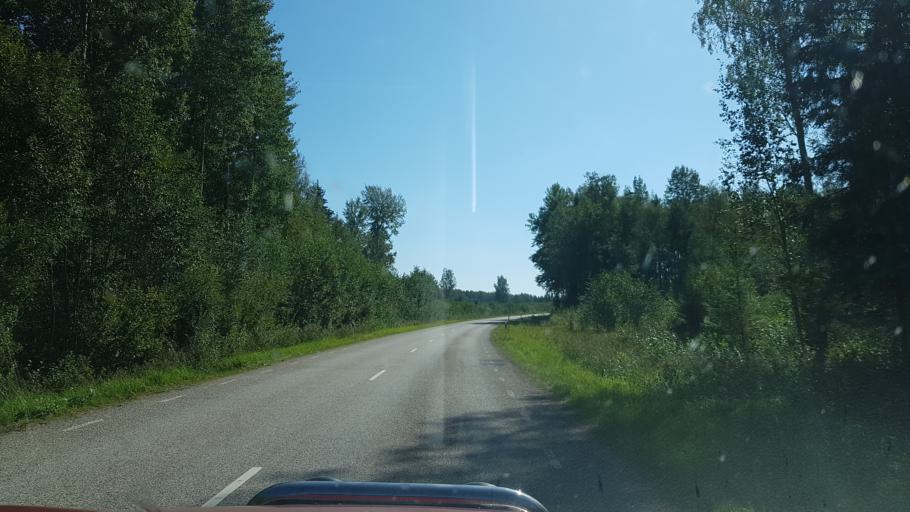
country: EE
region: Polvamaa
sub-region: Polva linn
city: Polva
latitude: 58.2625
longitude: 27.1745
